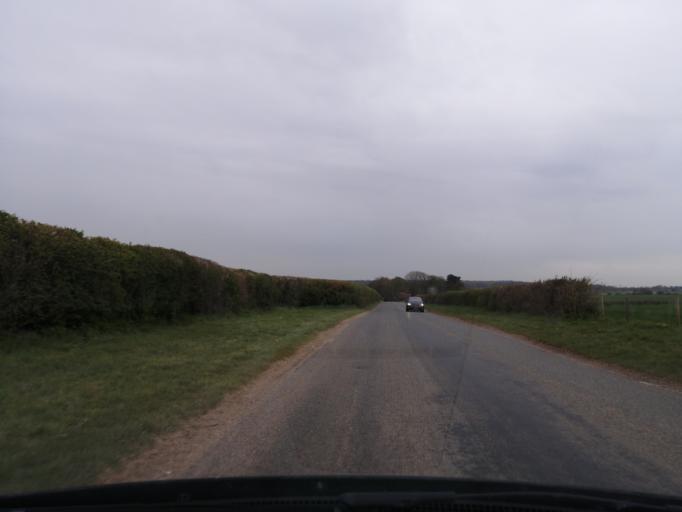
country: GB
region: England
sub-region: Peterborough
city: Wittering
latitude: 52.6062
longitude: -0.4620
